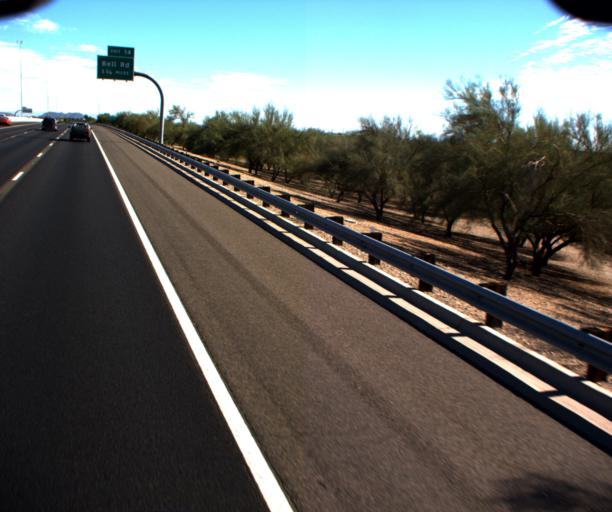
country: US
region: Arizona
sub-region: Maricopa County
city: Sun City
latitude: 33.6082
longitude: -112.2462
